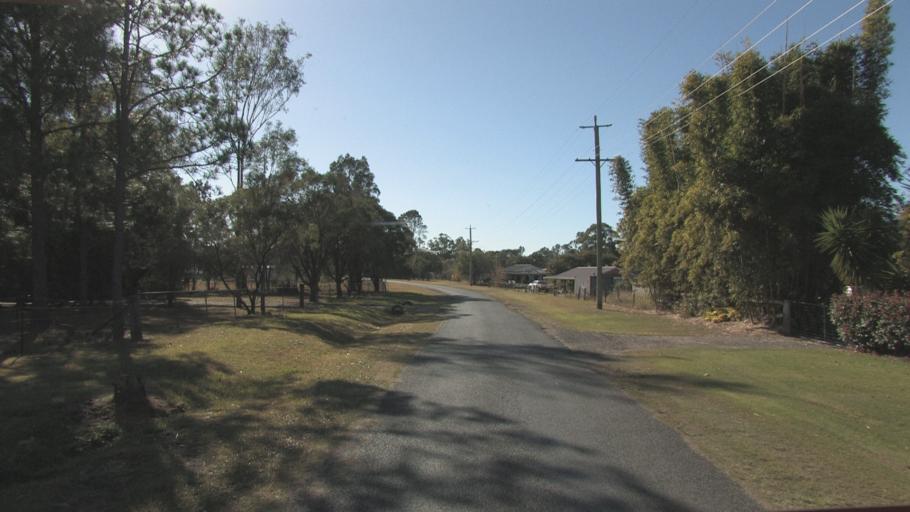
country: AU
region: Queensland
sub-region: Logan
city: Chambers Flat
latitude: -27.7627
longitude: 153.0494
